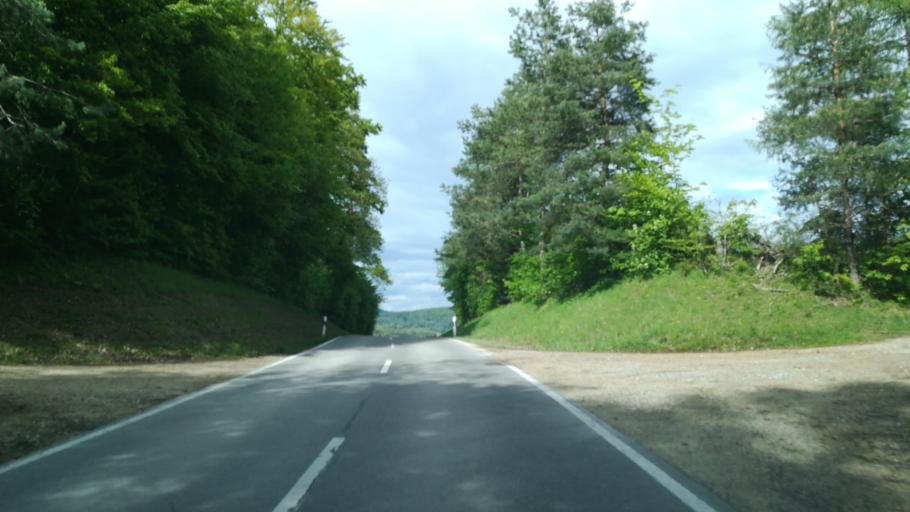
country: DE
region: Baden-Wuerttemberg
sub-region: Freiburg Region
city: Gailingen
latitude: 47.7182
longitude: 8.7385
